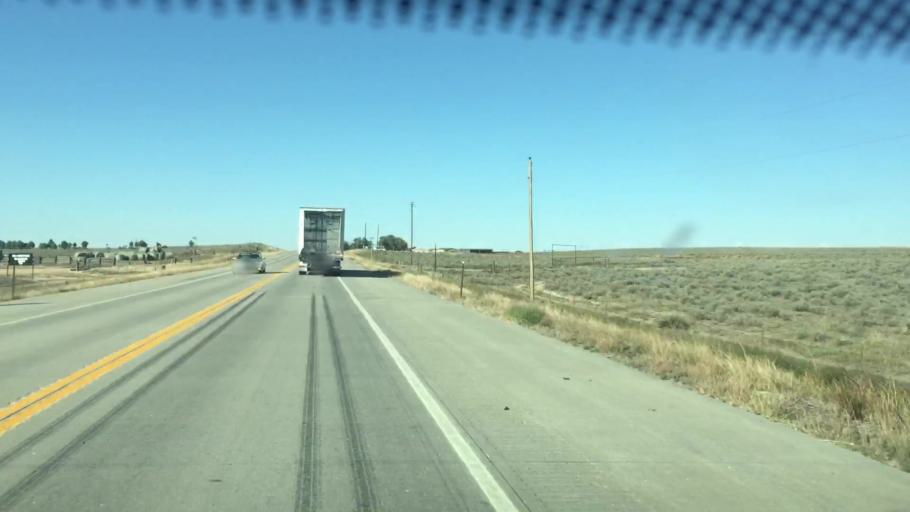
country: US
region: Colorado
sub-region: Kiowa County
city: Eads
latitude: 38.5841
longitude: -102.7860
